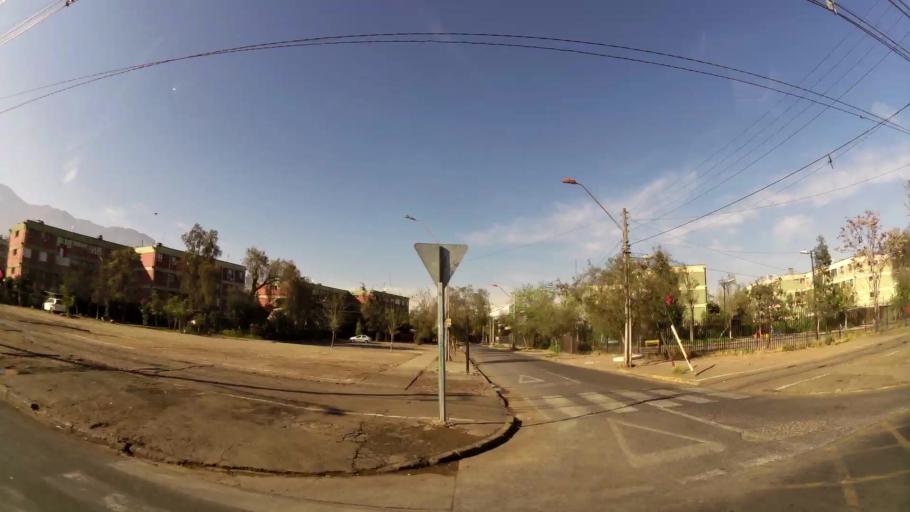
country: CL
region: Santiago Metropolitan
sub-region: Provincia de Santiago
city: Villa Presidente Frei, Nunoa, Santiago, Chile
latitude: -33.4626
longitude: -70.5535
